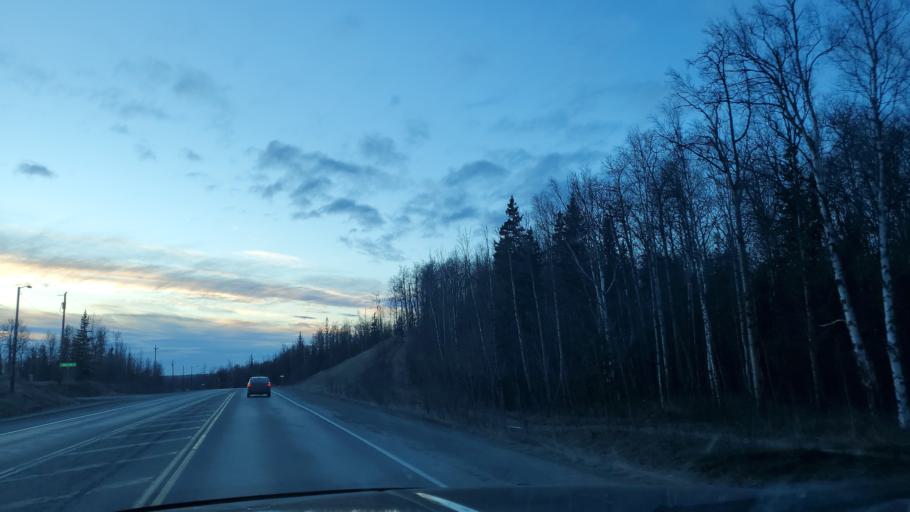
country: US
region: Alaska
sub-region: Matanuska-Susitna Borough
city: Wasilla
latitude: 61.5979
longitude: -149.4248
